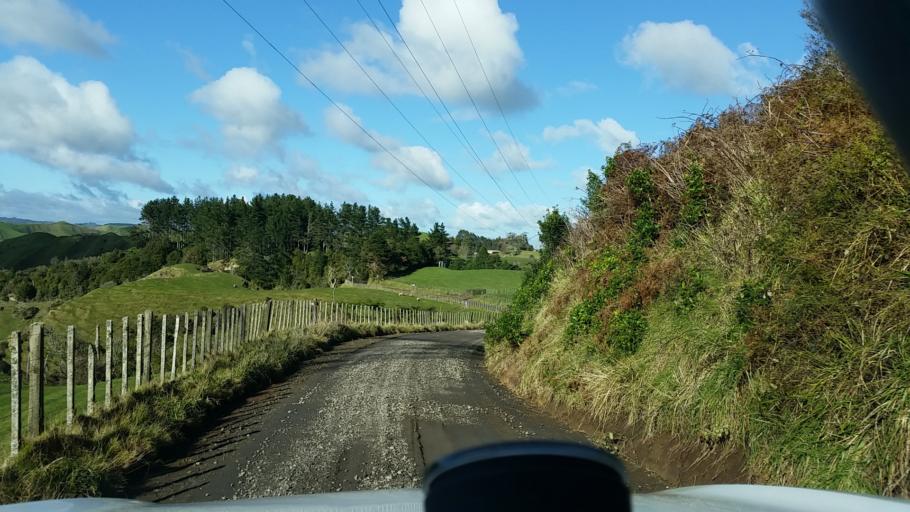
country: NZ
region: Taranaki
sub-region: South Taranaki District
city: Eltham
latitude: -39.4562
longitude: 174.3691
